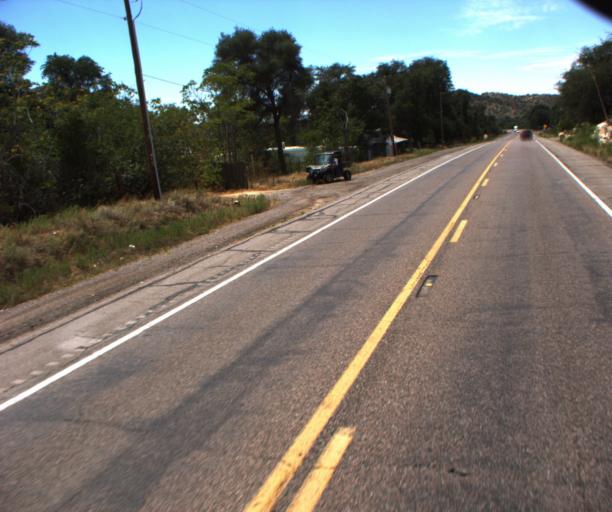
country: US
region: Arizona
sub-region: Gila County
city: Miami
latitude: 33.3528
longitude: -110.9850
